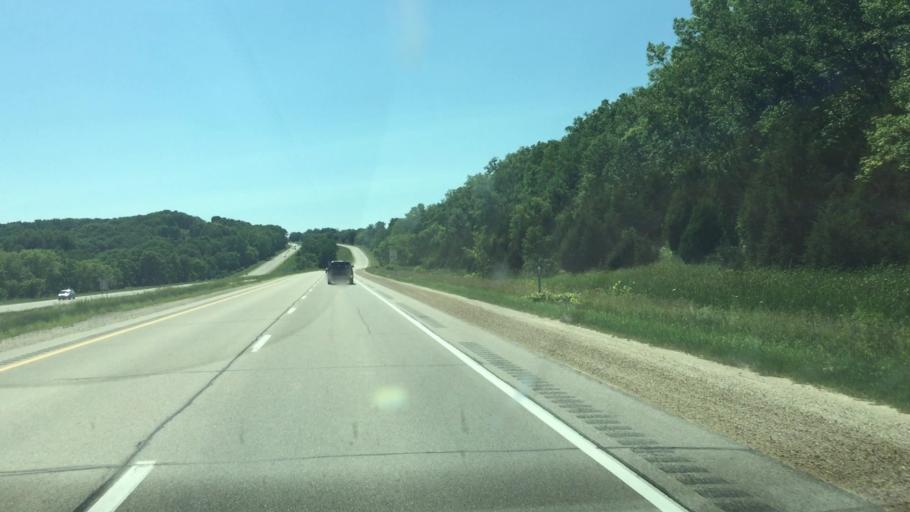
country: US
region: Iowa
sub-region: Dubuque County
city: Dubuque
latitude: 42.4187
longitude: -90.7050
